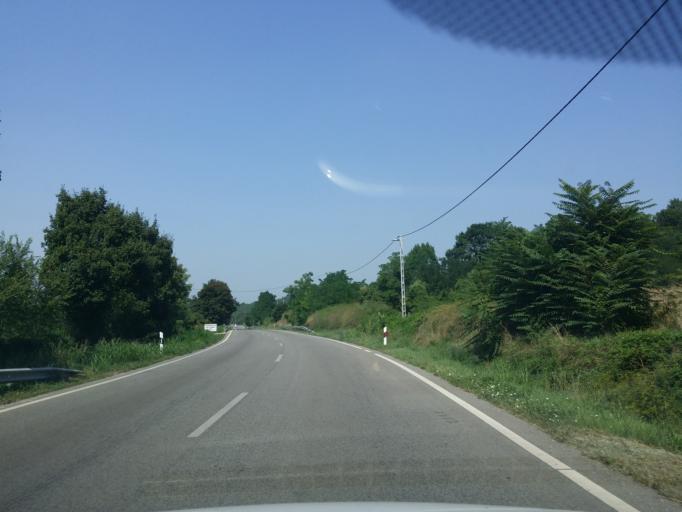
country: HU
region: Tolna
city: Pincehely
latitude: 46.7009
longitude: 18.4676
